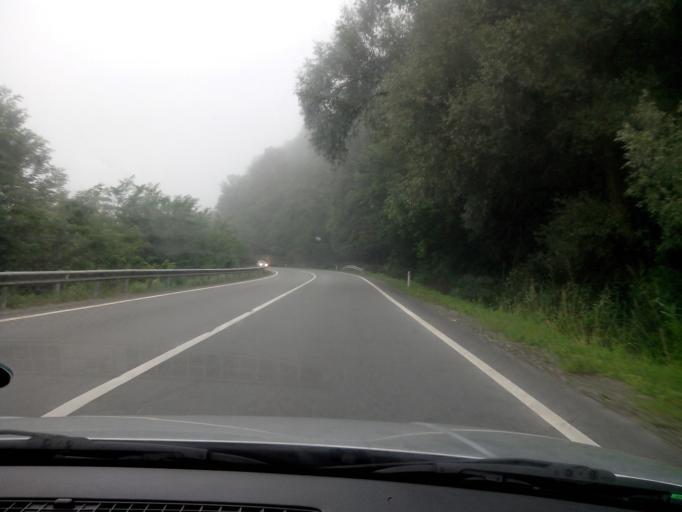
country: RO
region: Salaj
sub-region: Comuna Rus
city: Rus
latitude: 47.2842
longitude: 23.6102
